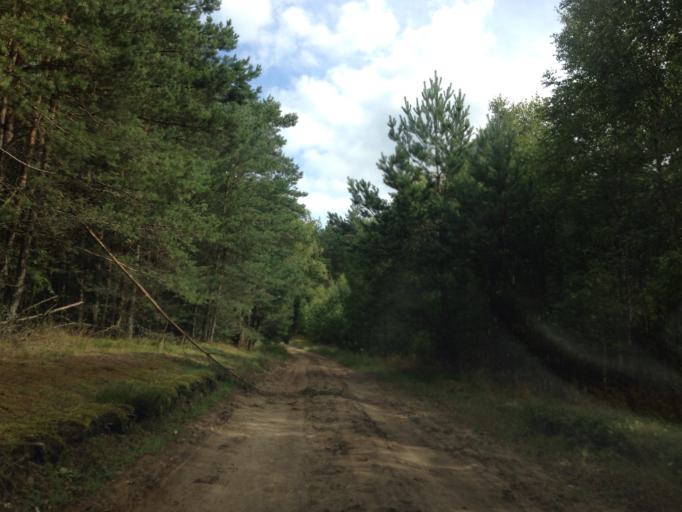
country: PL
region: Pomeranian Voivodeship
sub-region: Powiat bytowski
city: Studzienice
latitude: 54.0460
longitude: 17.6473
